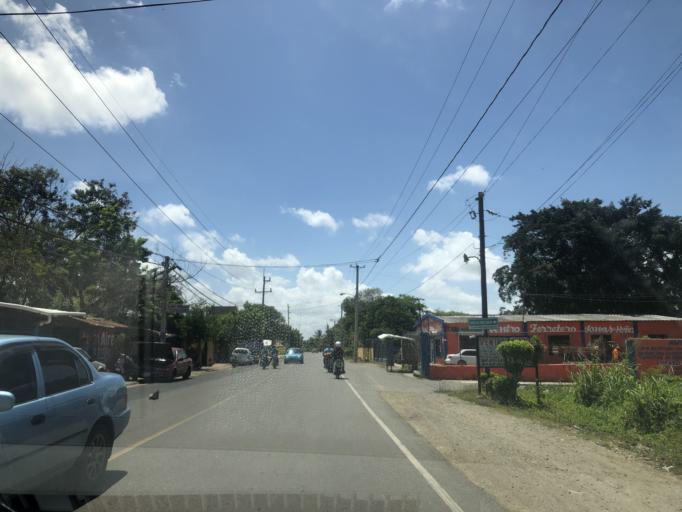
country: DO
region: Santiago
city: La Canela
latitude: 19.4508
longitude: -70.7751
